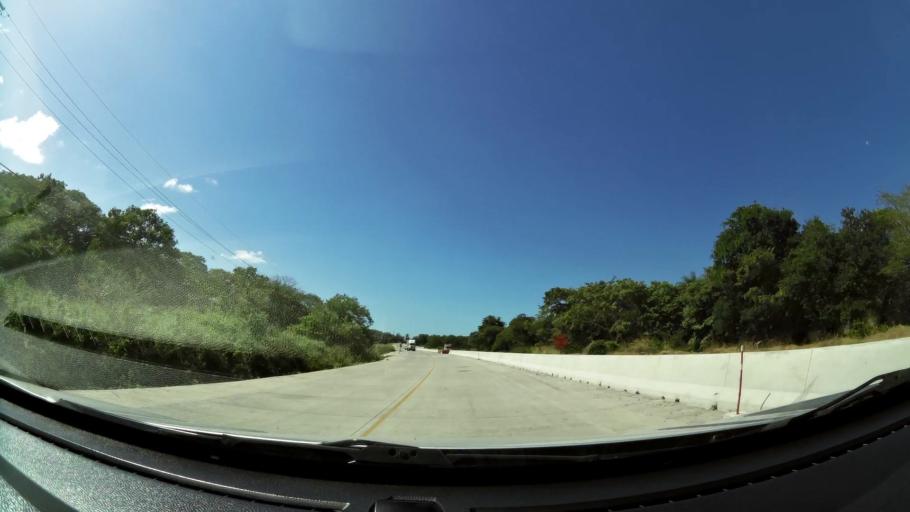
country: CR
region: Guanacaste
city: Bagaces
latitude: 10.5507
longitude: -85.3603
